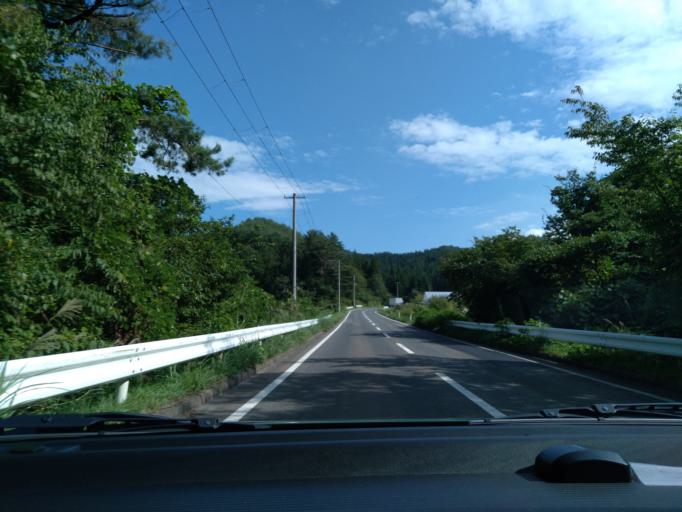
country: JP
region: Iwate
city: Shizukuishi
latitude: 39.6424
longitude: 141.0031
